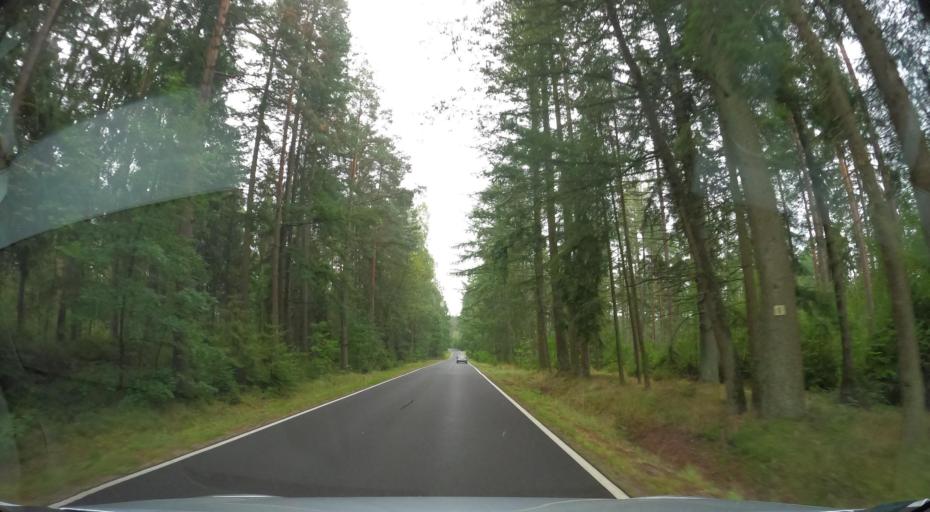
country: PL
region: Pomeranian Voivodeship
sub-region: Powiat wejherowski
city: Linia
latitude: 54.4885
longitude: 17.8433
